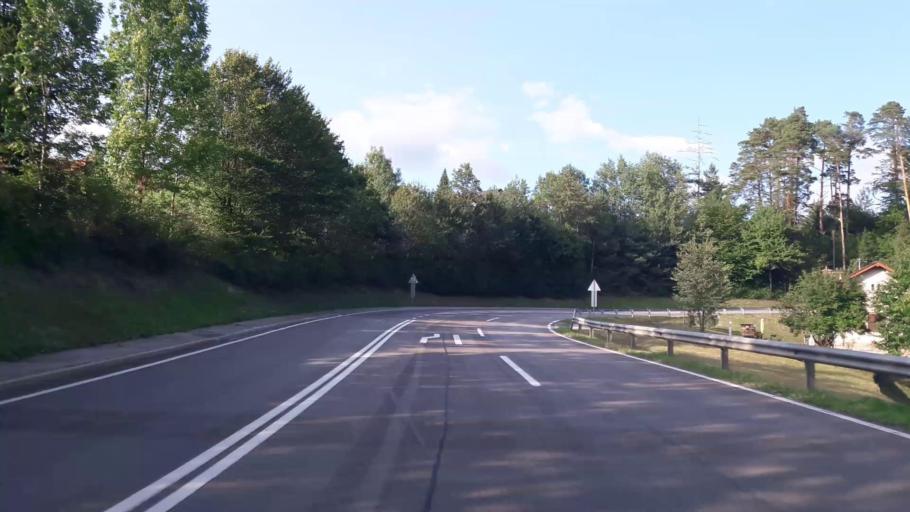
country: AT
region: Styria
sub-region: Politischer Bezirk Weiz
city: Anger
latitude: 47.2491
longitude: 15.6957
